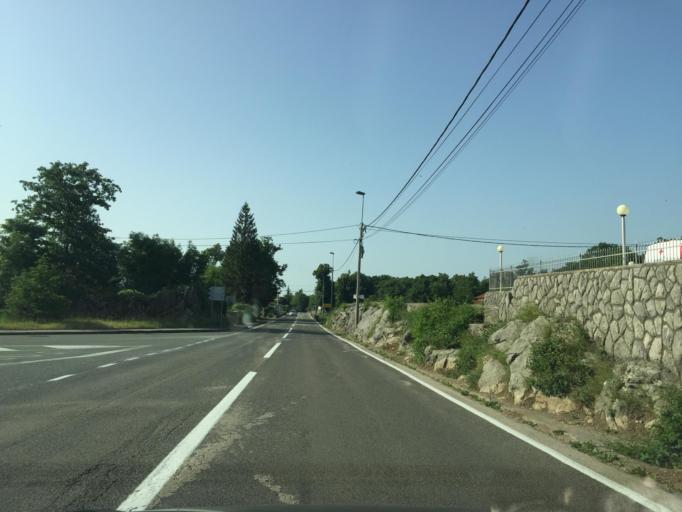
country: HR
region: Primorsko-Goranska
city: Matulji
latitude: 45.4103
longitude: 14.3032
